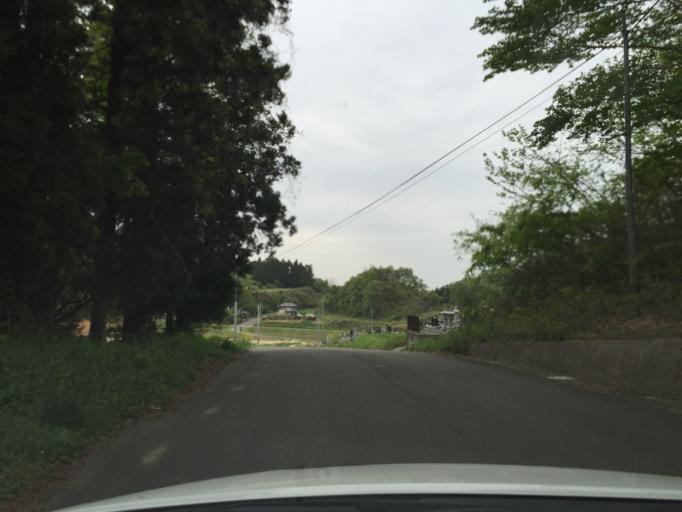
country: JP
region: Fukushima
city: Fukushima-shi
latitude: 37.6711
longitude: 140.4510
